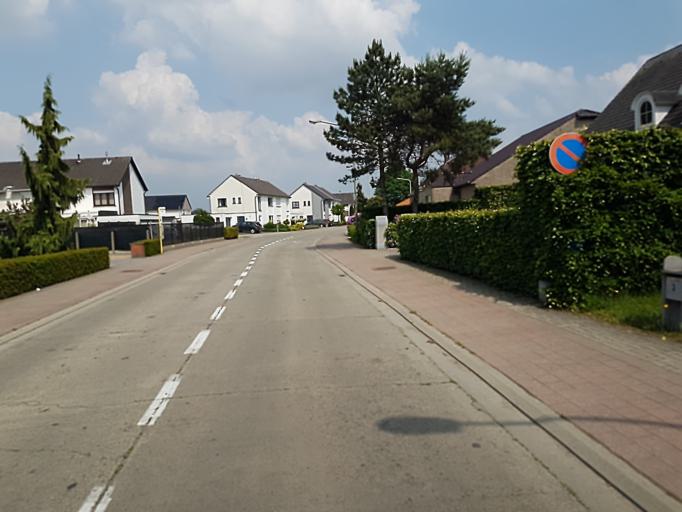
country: BE
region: Flanders
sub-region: Provincie Vlaams-Brabant
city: Londerzeel
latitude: 51.0111
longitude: 4.2983
